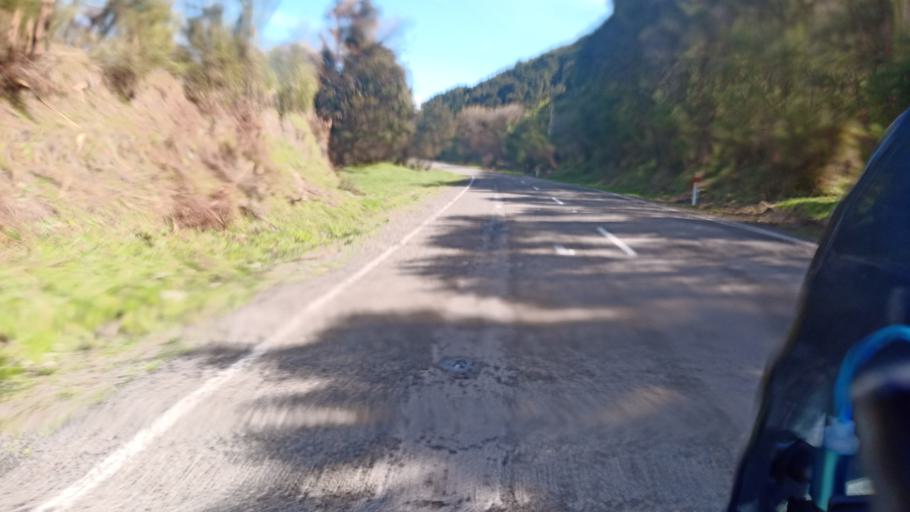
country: NZ
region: Gisborne
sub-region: Gisborne District
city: Gisborne
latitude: -37.8625
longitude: 178.1816
